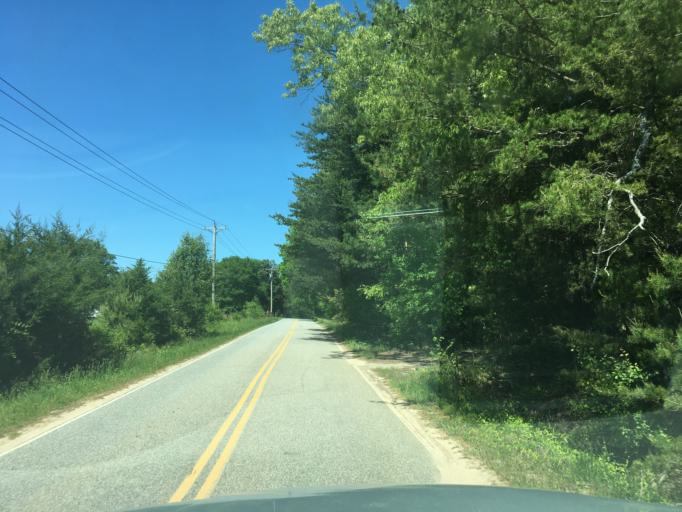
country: US
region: South Carolina
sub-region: Spartanburg County
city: Duncan
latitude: 34.8743
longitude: -82.1779
